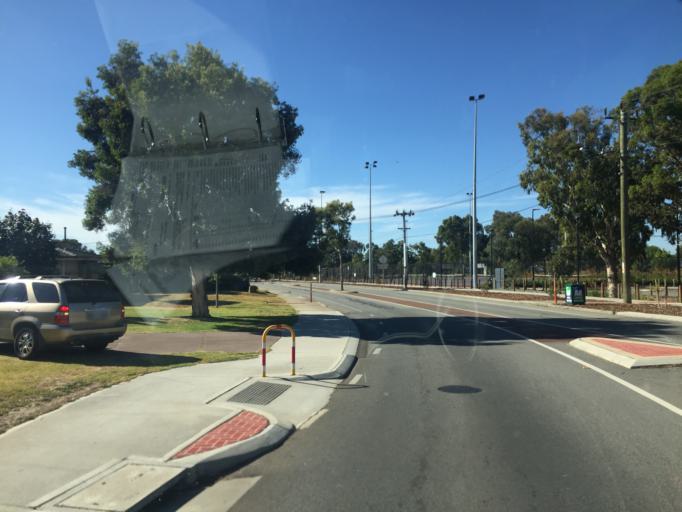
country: AU
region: Western Australia
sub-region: Gosnells
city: Kenwick
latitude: -32.0236
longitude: 115.9657
